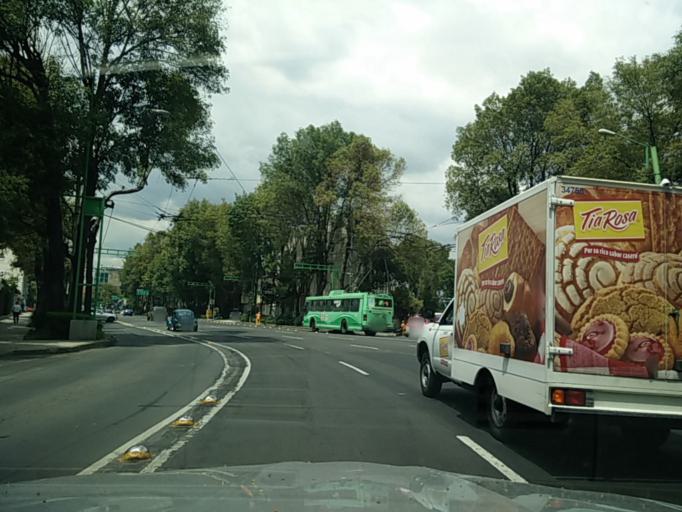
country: MX
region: Mexico City
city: Coyoacan
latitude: 19.3591
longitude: -99.1519
